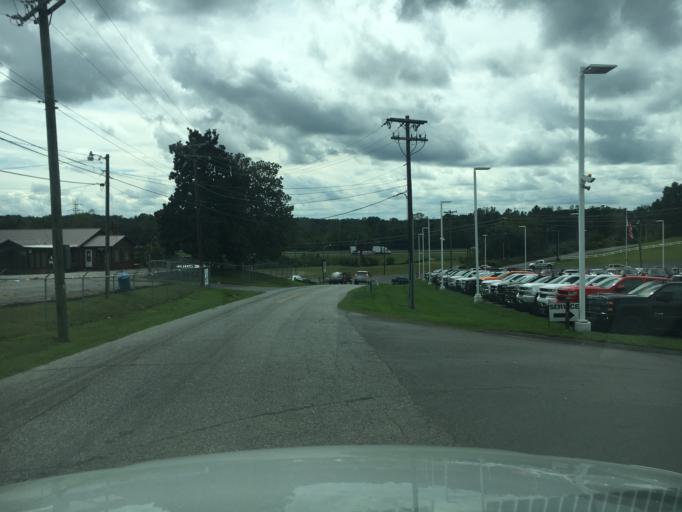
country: US
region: North Carolina
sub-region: Catawba County
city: Hickory
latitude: 35.7149
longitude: -81.3328
